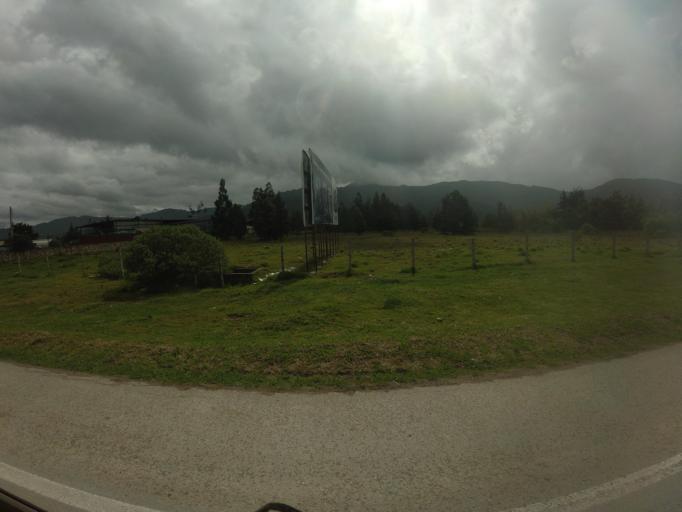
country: CO
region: Boyaca
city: Tibasosa
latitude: 5.7886
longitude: -72.9853
